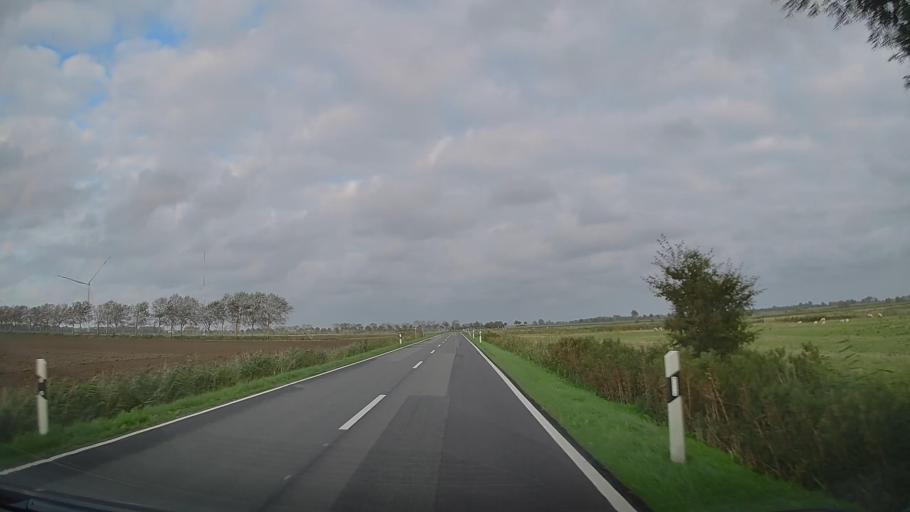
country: DE
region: Schleswig-Holstein
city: Husum
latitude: 54.4393
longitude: 9.0289
